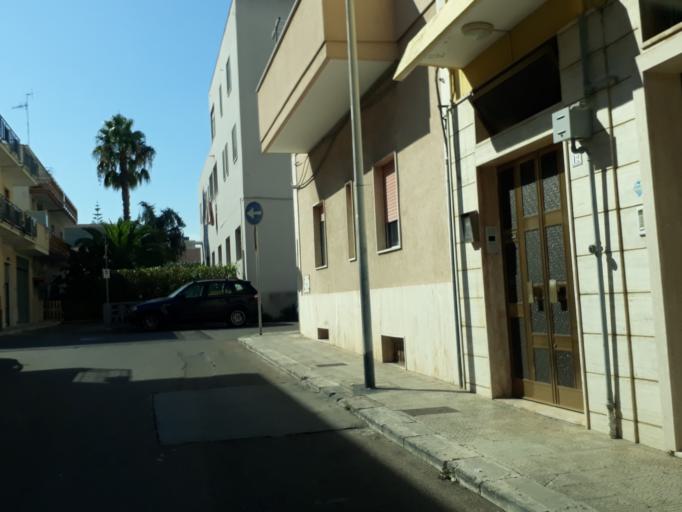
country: IT
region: Apulia
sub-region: Provincia di Bari
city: Monopoli
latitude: 40.9488
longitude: 17.2944
